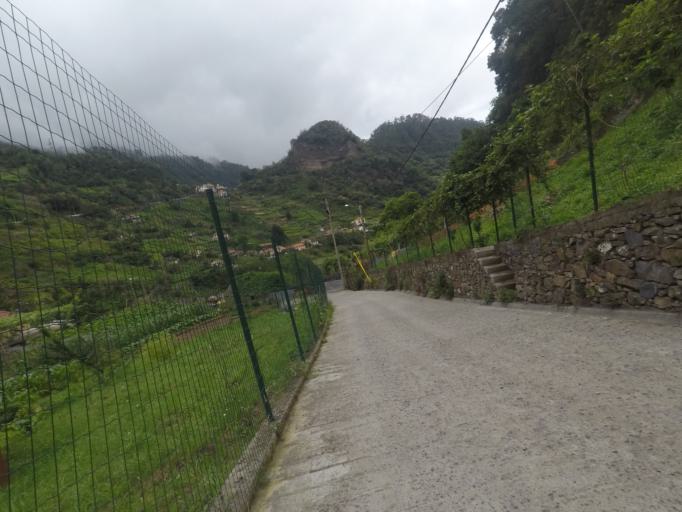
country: PT
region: Madeira
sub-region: Santana
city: Santana
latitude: 32.7546
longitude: -16.8769
